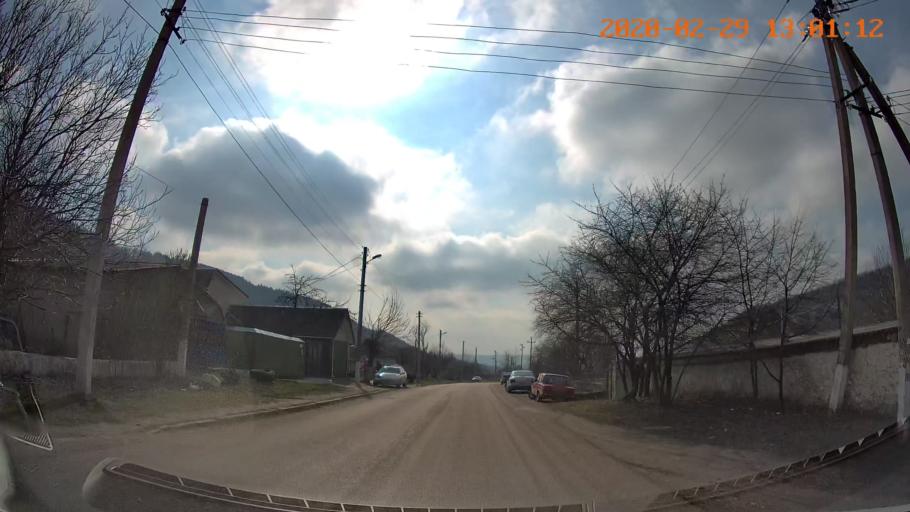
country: MD
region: Telenesti
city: Camenca
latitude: 48.0459
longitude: 28.7196
